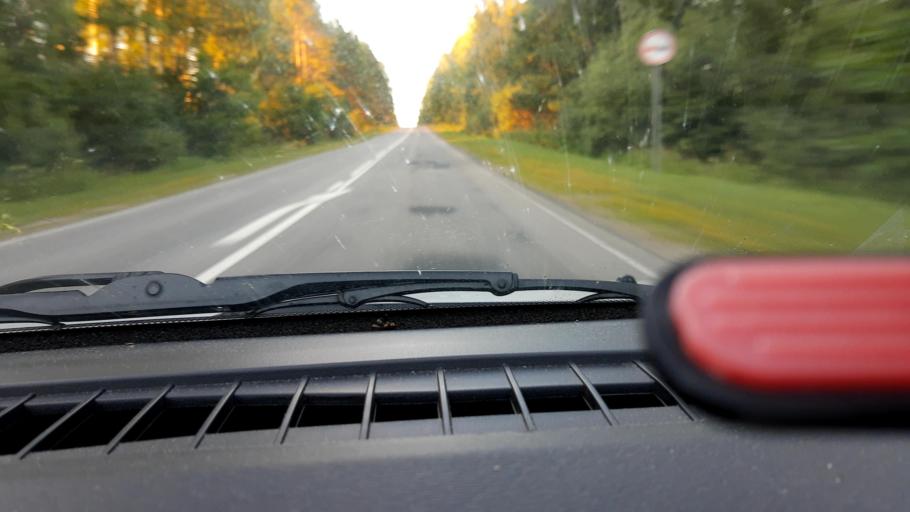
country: RU
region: Nizjnij Novgorod
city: Uren'
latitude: 57.3076
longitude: 45.6767
